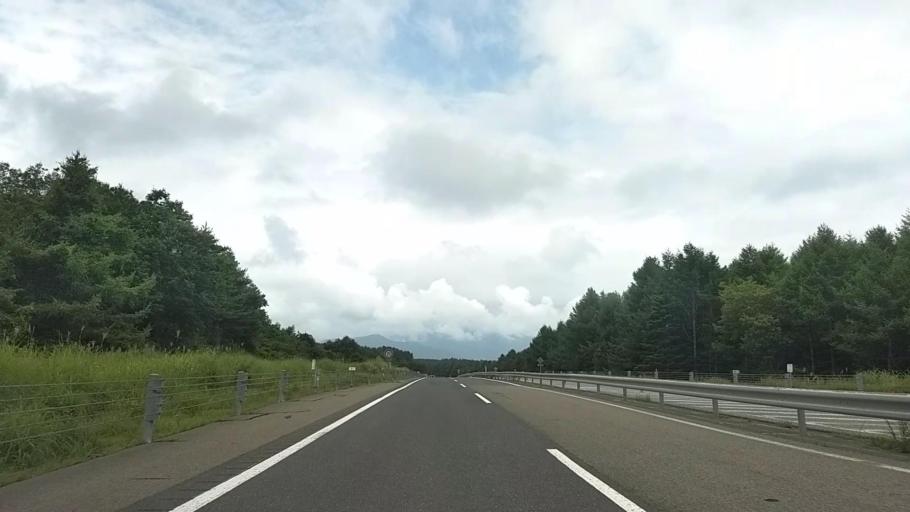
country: JP
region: Yamanashi
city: Fujikawaguchiko
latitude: 35.4502
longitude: 138.8012
